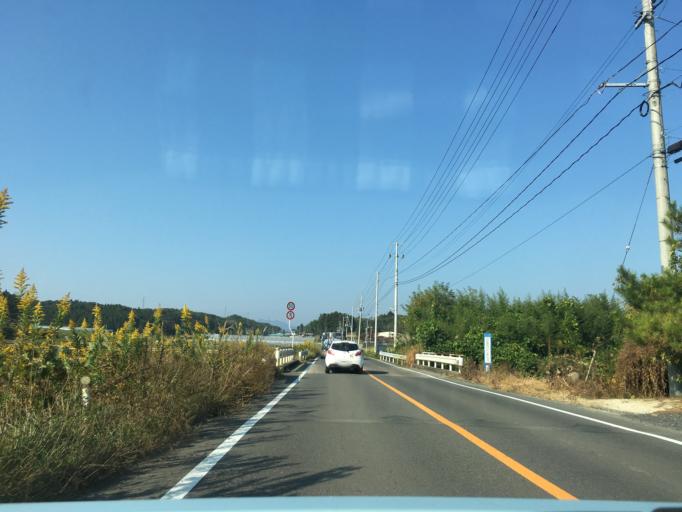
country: JP
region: Fukushima
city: Sukagawa
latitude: 37.2801
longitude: 140.3097
